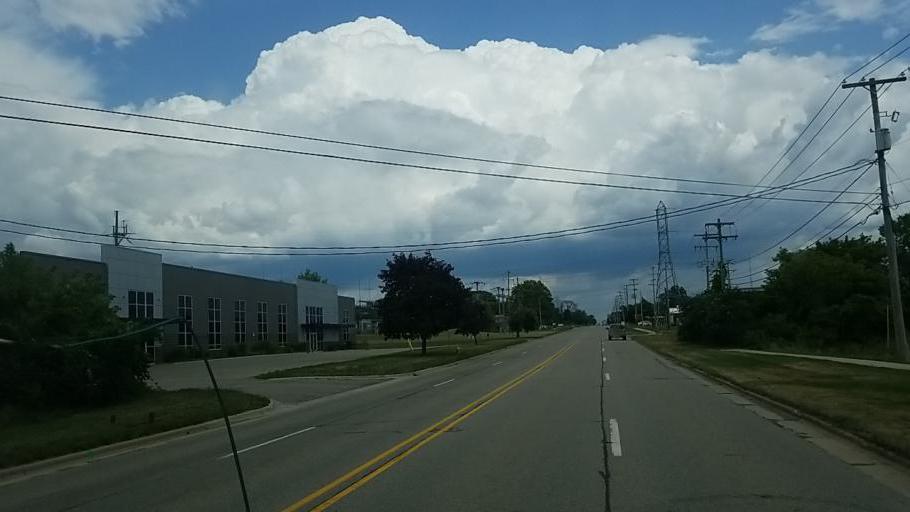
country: US
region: Michigan
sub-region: Kent County
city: Walker
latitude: 43.0158
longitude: -85.7596
